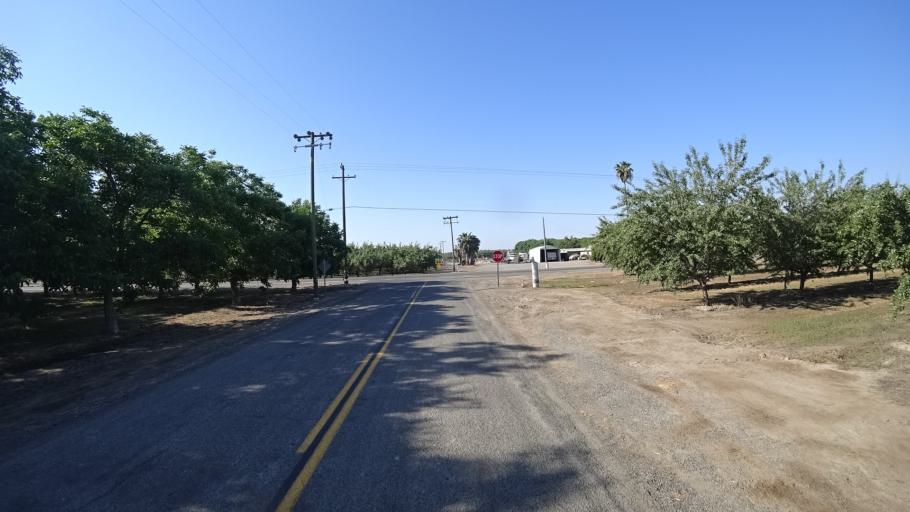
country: US
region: California
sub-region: Fresno County
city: Laton
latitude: 36.4015
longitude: -119.7134
